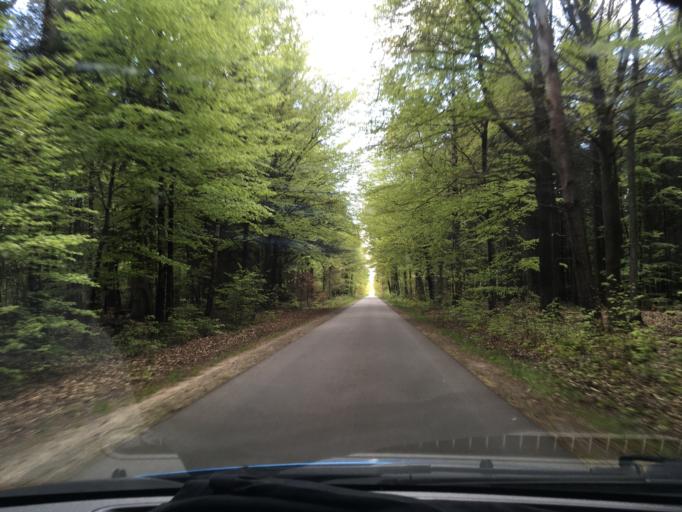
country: DE
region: Lower Saxony
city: Nahrendorf
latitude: 53.1324
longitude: 10.7988
